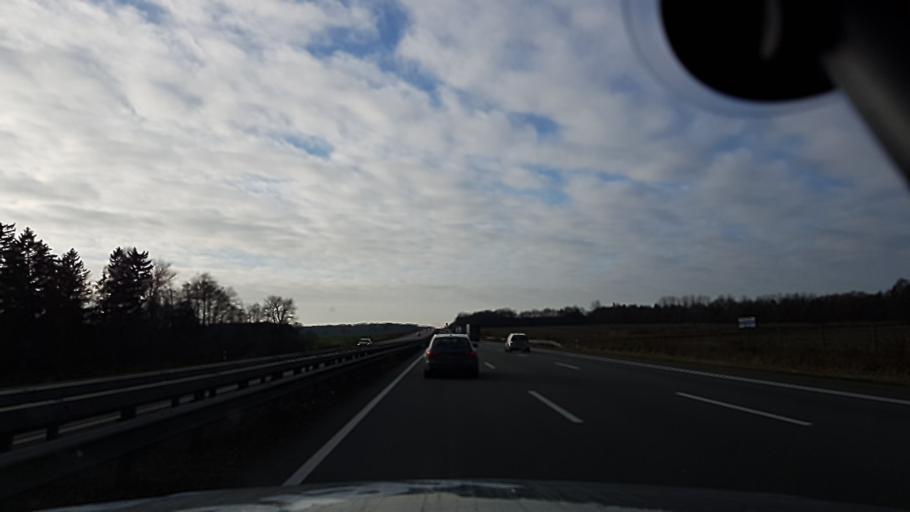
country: DE
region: Lower Saxony
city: Kalbe
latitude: 53.3134
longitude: 9.5652
